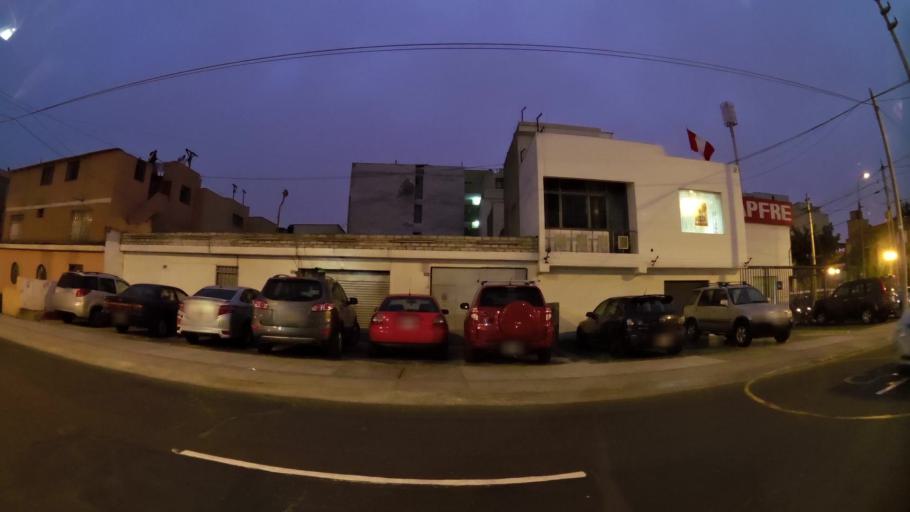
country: PE
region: Callao
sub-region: Callao
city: Callao
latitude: -12.0792
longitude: -77.0942
